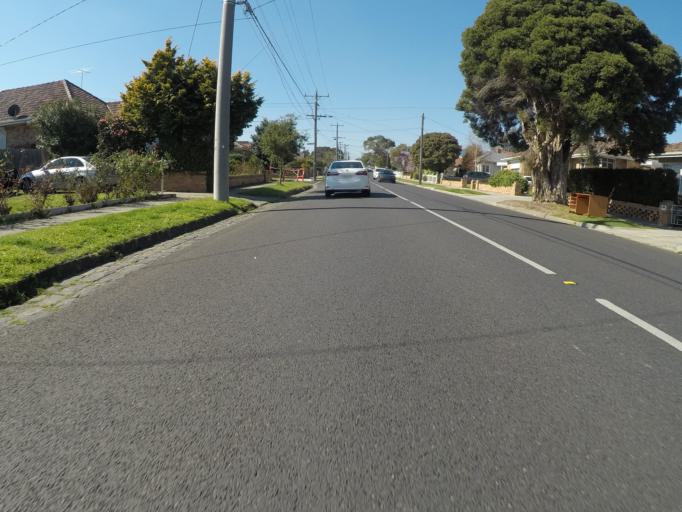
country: AU
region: Victoria
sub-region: Moreland
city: Pascoe Vale South
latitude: -37.7460
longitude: 144.9398
